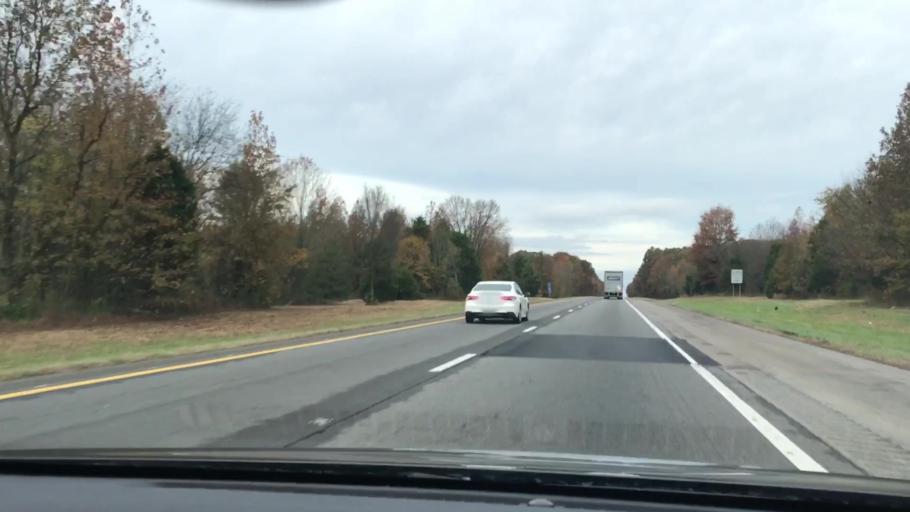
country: US
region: Tennessee
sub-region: Cheatham County
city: Pleasant View
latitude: 36.4131
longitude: -87.0428
